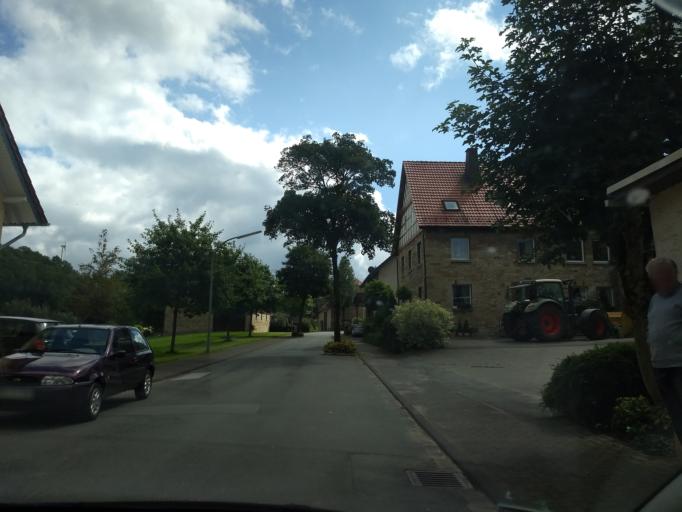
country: DE
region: North Rhine-Westphalia
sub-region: Regierungsbezirk Detmold
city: Buren
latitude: 51.5393
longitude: 8.5250
